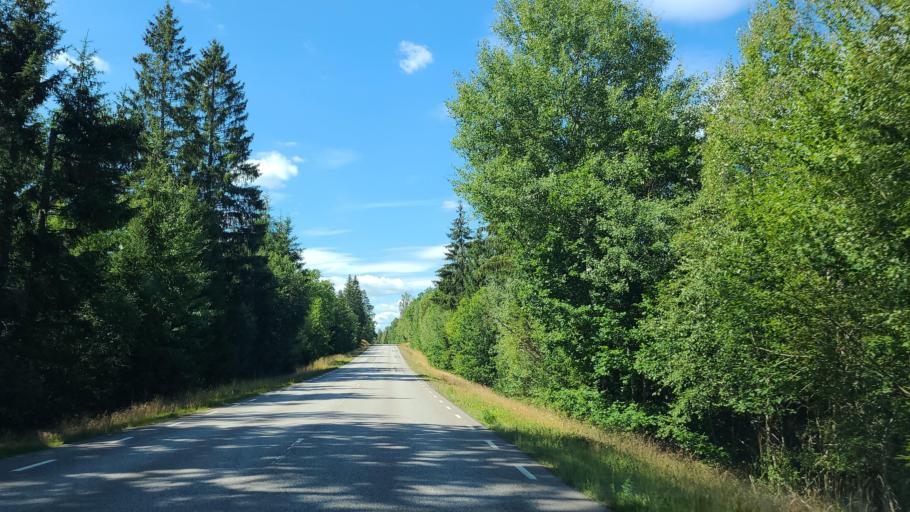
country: SE
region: Kalmar
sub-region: Emmaboda Kommun
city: Emmaboda
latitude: 56.5404
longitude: 15.6706
